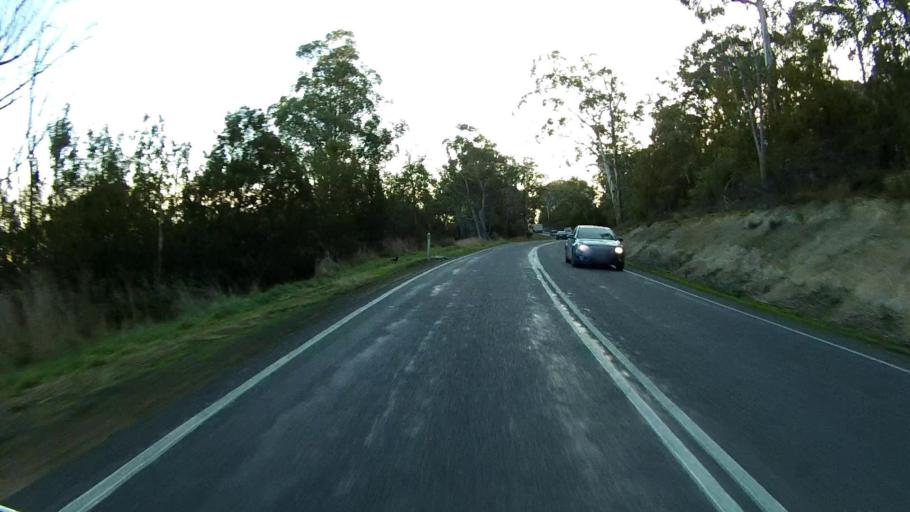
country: AU
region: Tasmania
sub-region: Sorell
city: Sorell
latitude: -42.8139
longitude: 147.6602
